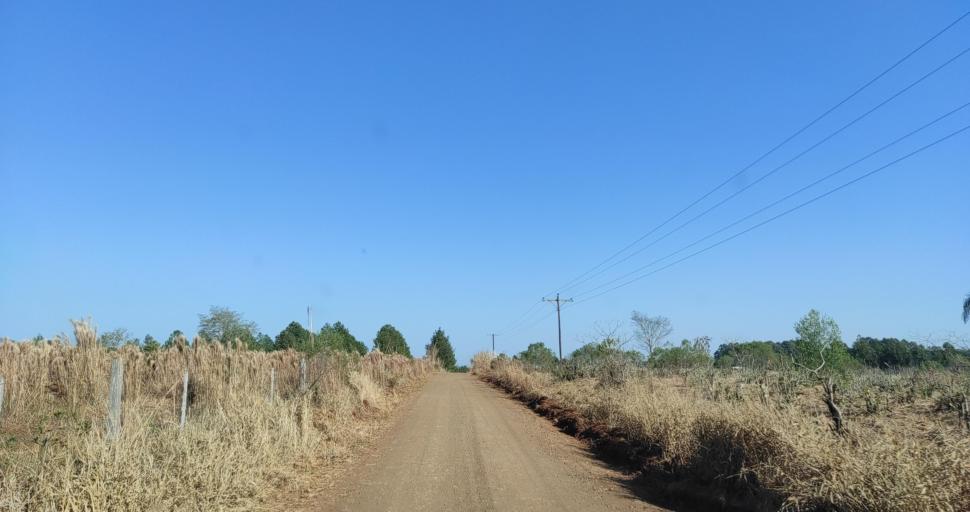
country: AR
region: Misiones
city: Capiovi
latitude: -26.8937
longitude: -55.0450
